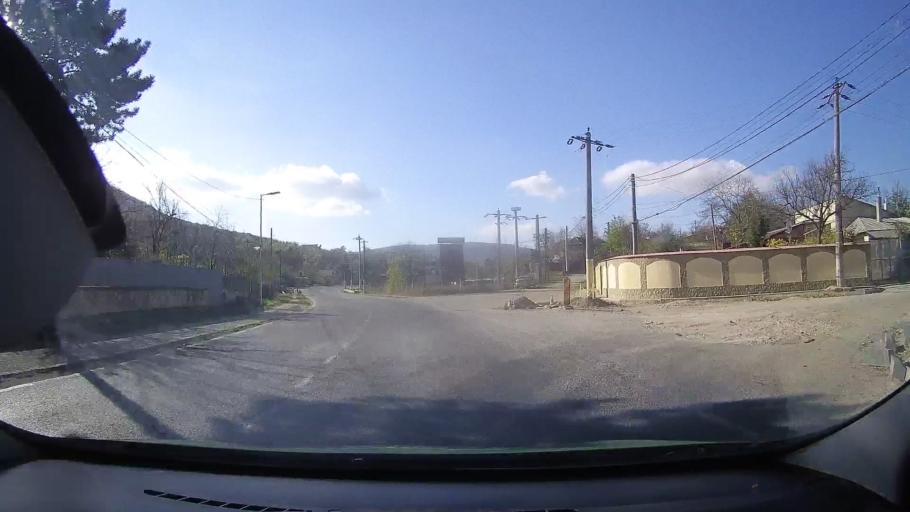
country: RO
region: Tulcea
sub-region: Oras Babadag
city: Babadag
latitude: 44.8848
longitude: 28.7015
